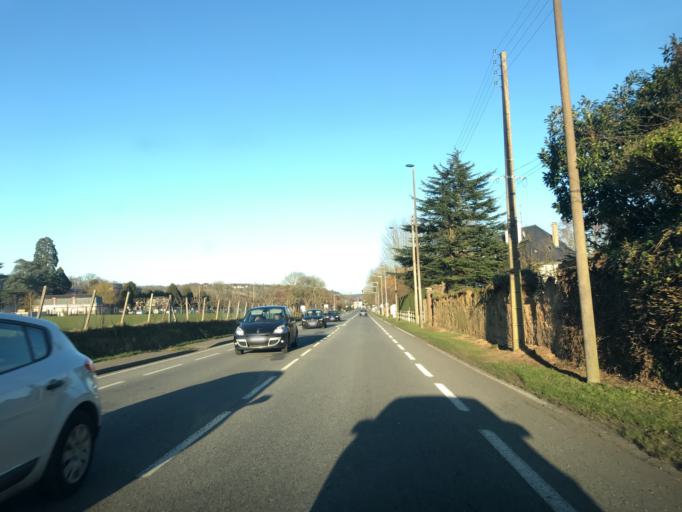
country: FR
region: Haute-Normandie
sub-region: Departement de l'Eure
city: Arnieres-sur-Iton
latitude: 49.0164
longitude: 1.1120
